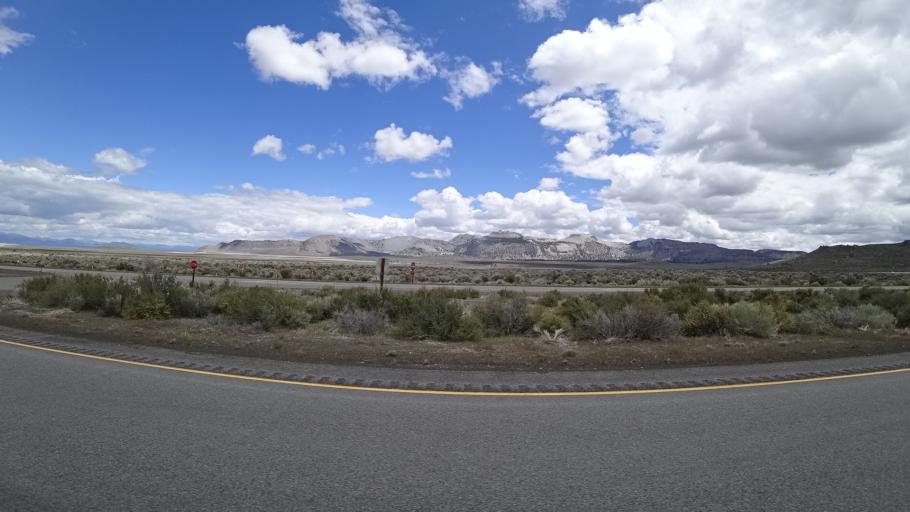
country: US
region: California
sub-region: Mono County
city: Mammoth Lakes
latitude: 37.8741
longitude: -119.0889
